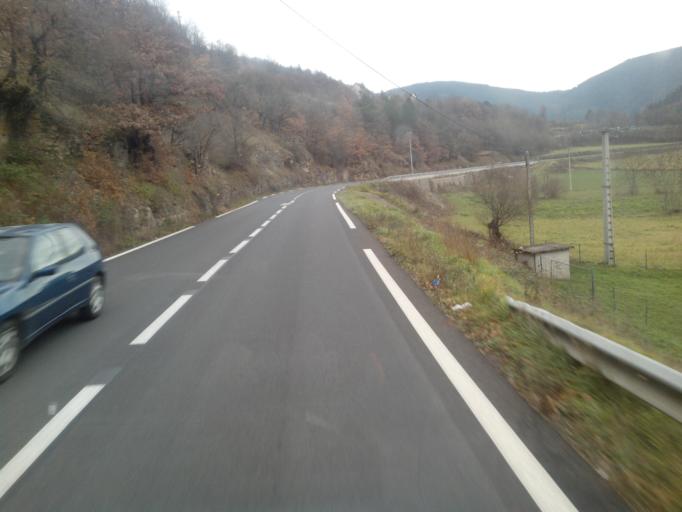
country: FR
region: Languedoc-Roussillon
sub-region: Departement de la Lozere
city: Mende
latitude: 44.4802
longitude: 3.4606
